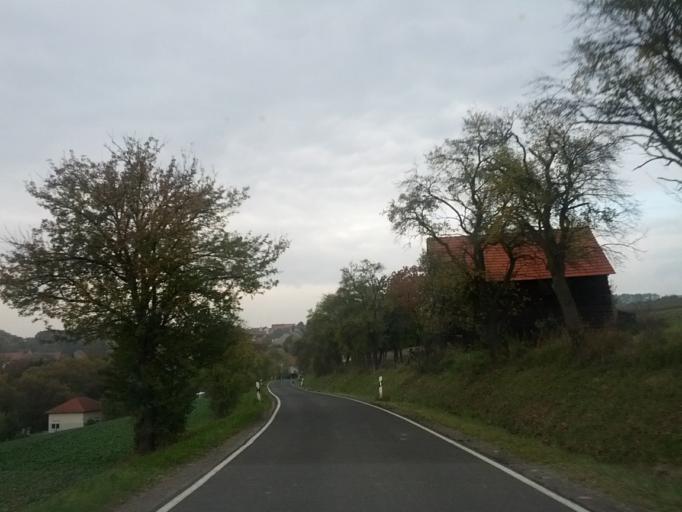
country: DE
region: Hesse
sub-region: Regierungsbezirk Kassel
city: Herleshausen
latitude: 51.0352
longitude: 10.1891
